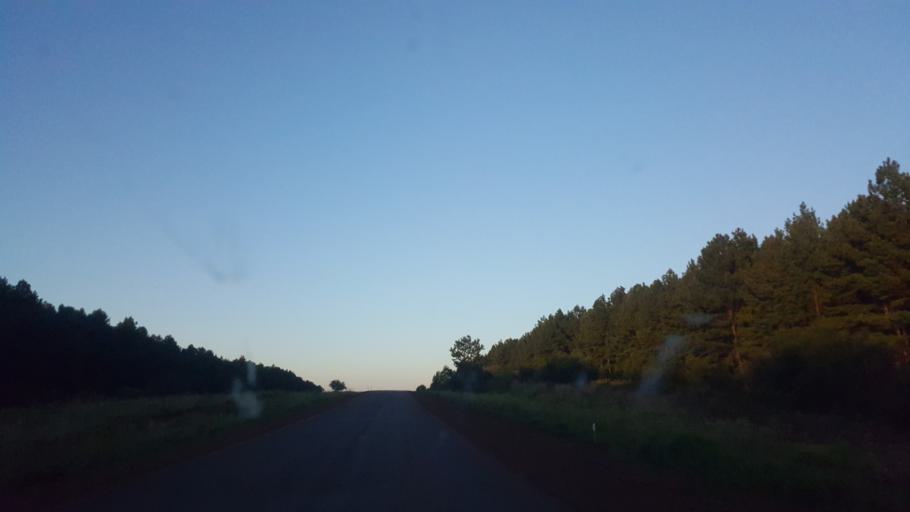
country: AR
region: Corrientes
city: Santo Tome
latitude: -28.4222
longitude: -55.9898
